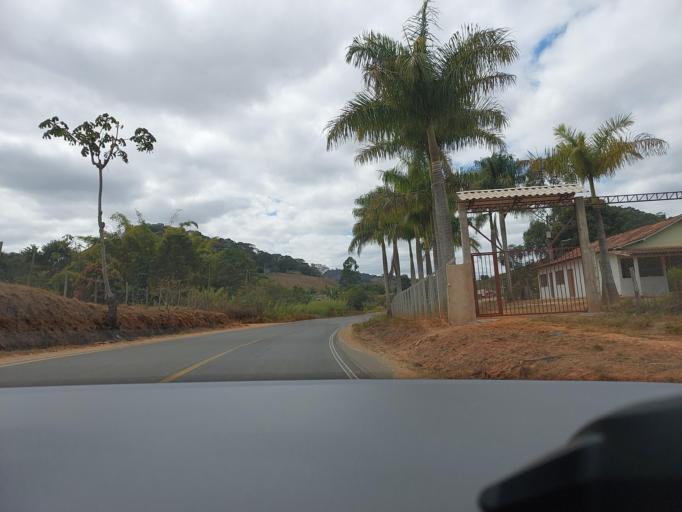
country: BR
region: Minas Gerais
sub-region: Vicosa
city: Vicosa
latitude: -20.8256
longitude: -42.7342
